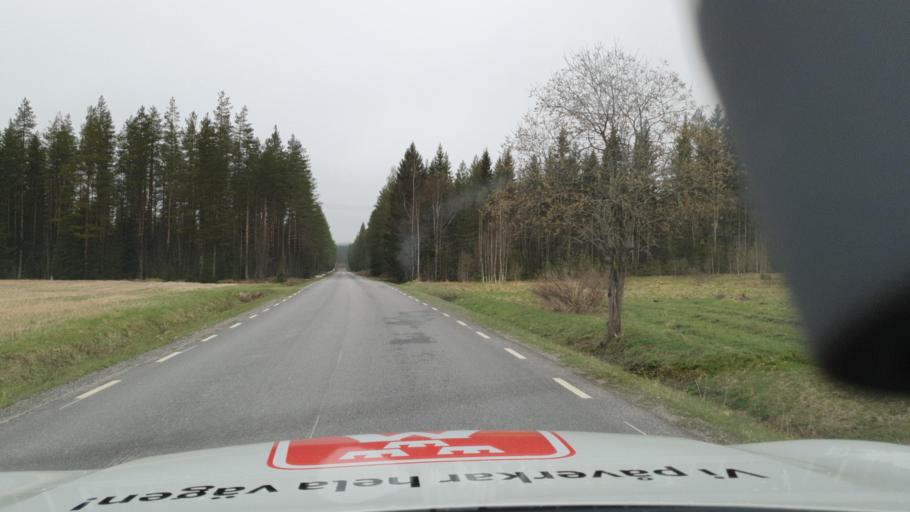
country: SE
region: Vaesterbotten
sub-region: Nordmalings Kommun
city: Nordmaling
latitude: 63.7164
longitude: 19.5717
